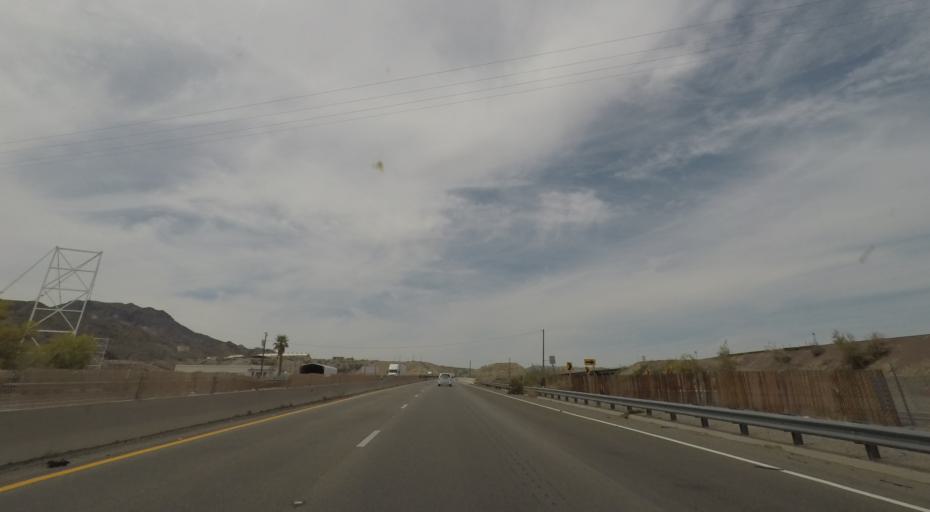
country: US
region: California
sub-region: San Bernardino County
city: Needles
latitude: 34.7177
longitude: -114.4837
